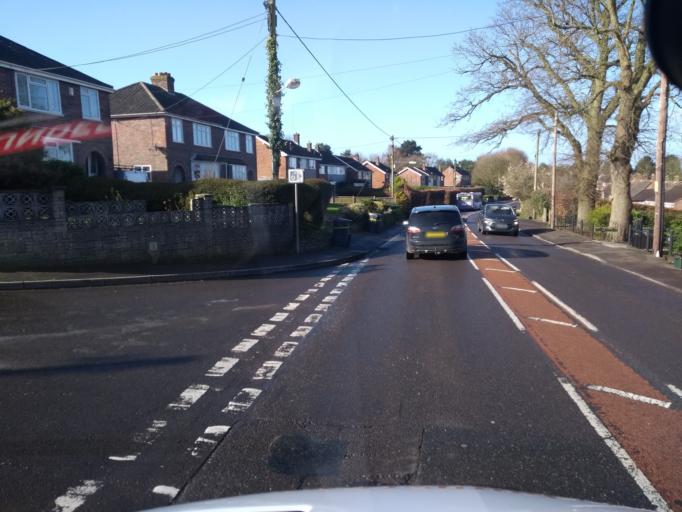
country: GB
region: England
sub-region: Somerset
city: Yeovil
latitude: 50.9566
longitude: -2.6363
